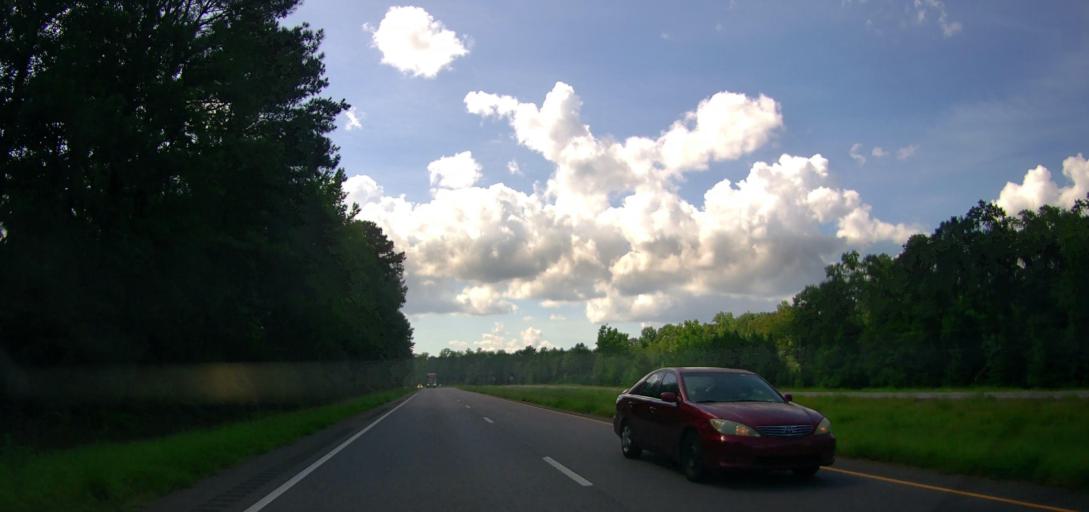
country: US
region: Alabama
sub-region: Pickens County
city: Reform
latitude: 33.3686
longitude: -87.9859
